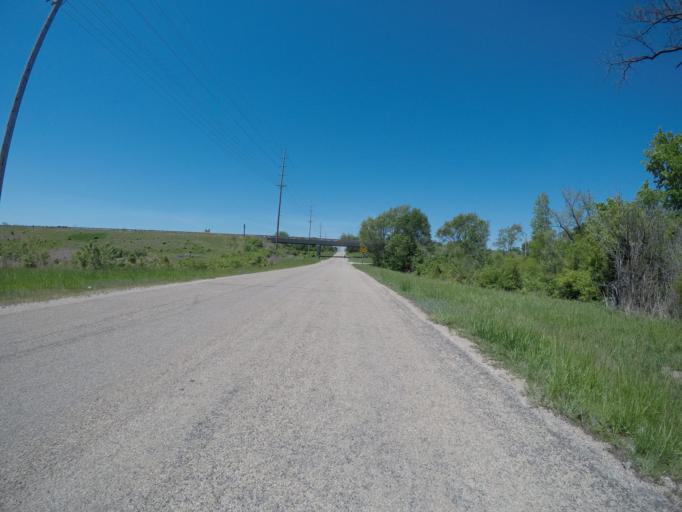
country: US
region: Kansas
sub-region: Shawnee County
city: Topeka
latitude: 39.0517
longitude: -95.6022
